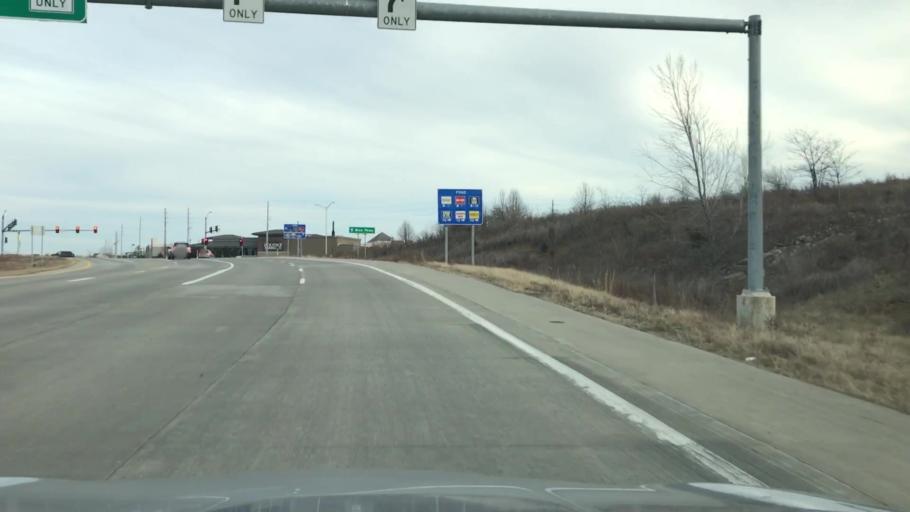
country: US
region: Missouri
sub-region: Jackson County
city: Lees Summit
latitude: 38.9331
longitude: -94.4141
